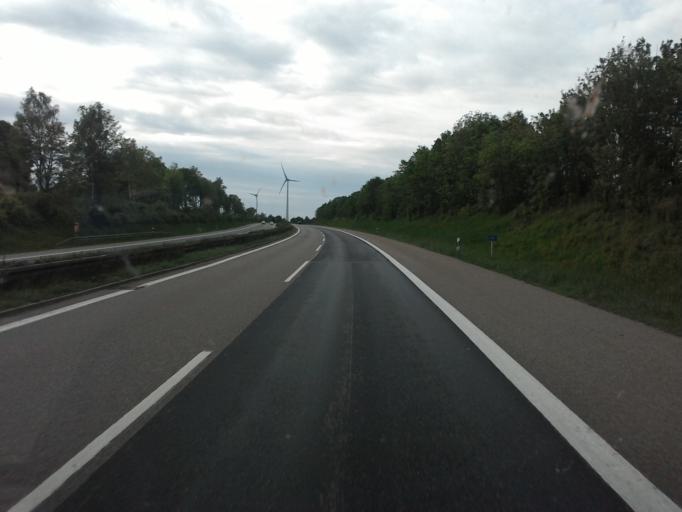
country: DE
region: Bavaria
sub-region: Upper Palatinate
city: Pilsach
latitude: 49.2934
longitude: 11.5574
